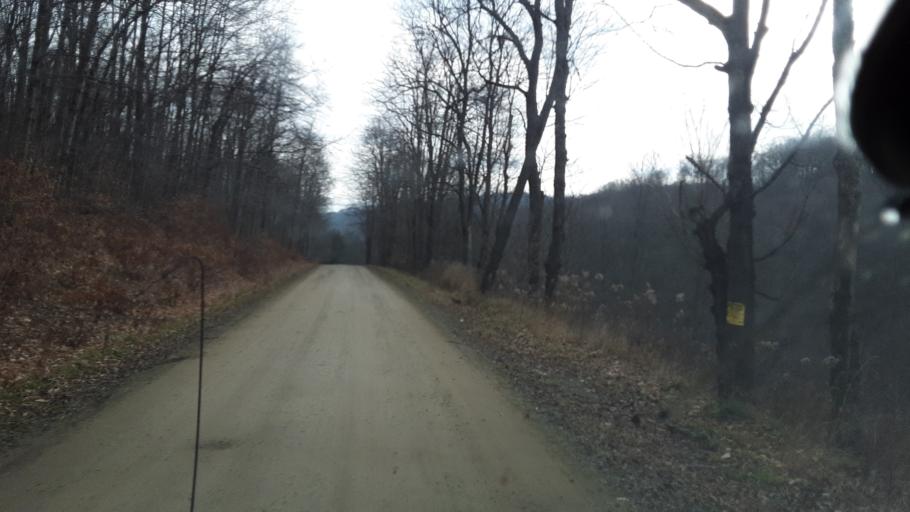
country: US
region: Pennsylvania
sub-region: Tioga County
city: Westfield
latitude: 41.9078
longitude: -77.7177
